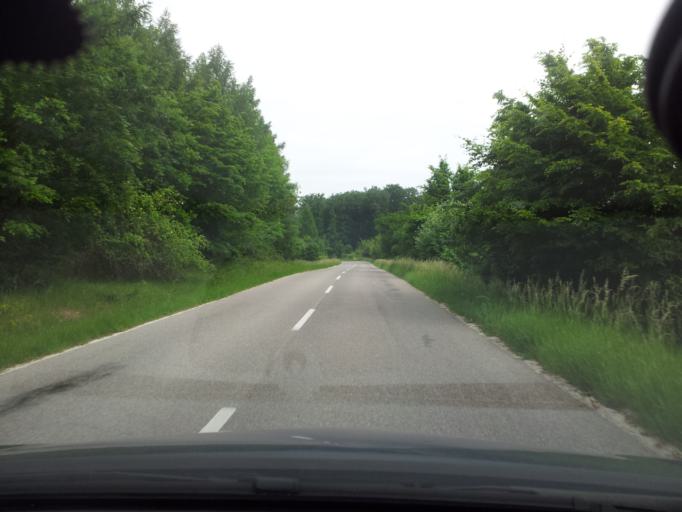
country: SK
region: Nitriansky
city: Partizanske
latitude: 48.5435
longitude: 18.4421
